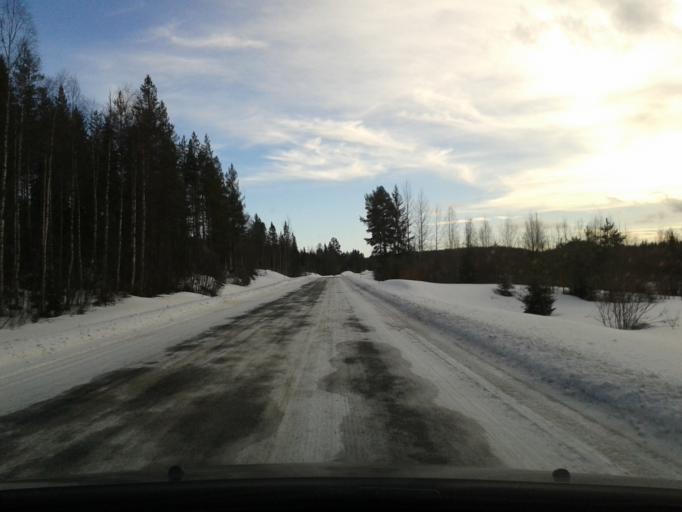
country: SE
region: Vaesterbotten
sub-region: Asele Kommun
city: Asele
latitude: 64.2227
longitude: 17.3064
